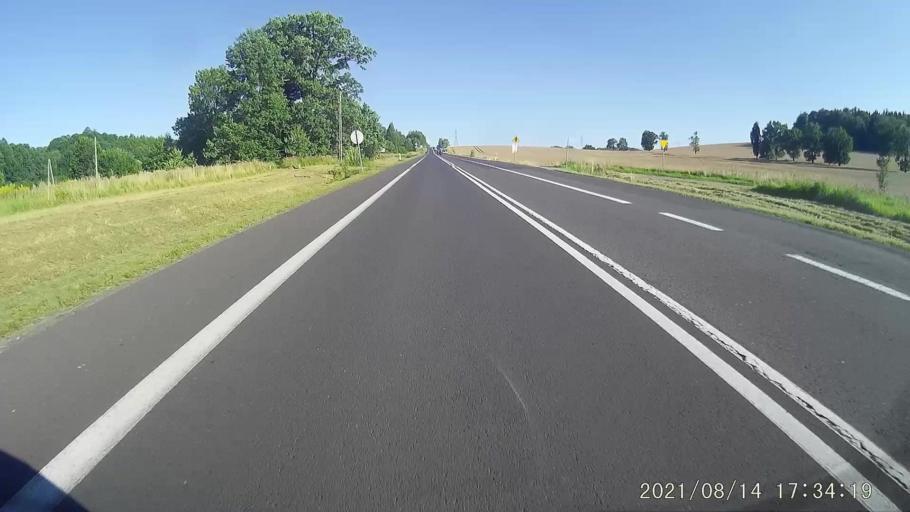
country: PL
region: Lower Silesian Voivodeship
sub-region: Powiat jeleniogorski
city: Stara Kamienica
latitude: 50.9350
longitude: 15.5998
